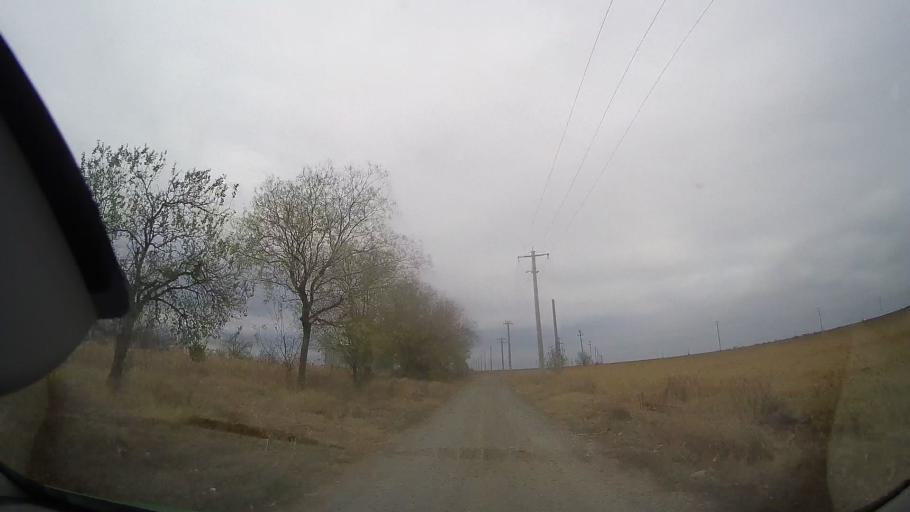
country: RO
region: Ialomita
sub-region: Comuna Milosesti
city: Milosesti
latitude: 44.7562
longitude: 27.2075
